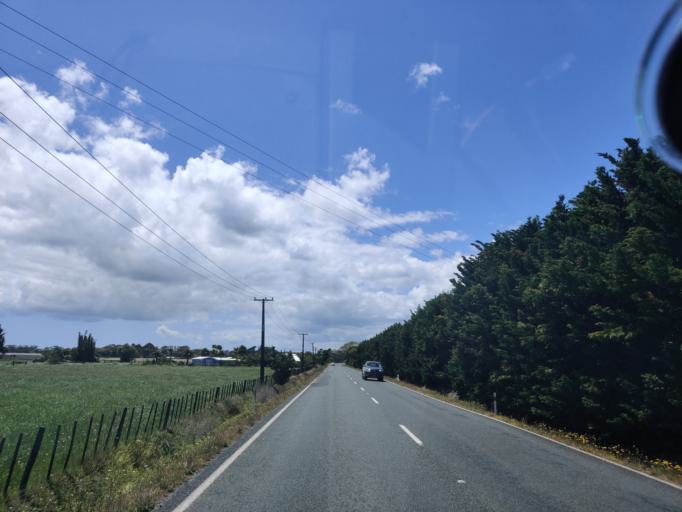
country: NZ
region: Northland
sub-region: Far North District
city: Kaitaia
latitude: -35.0257
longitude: 173.2446
